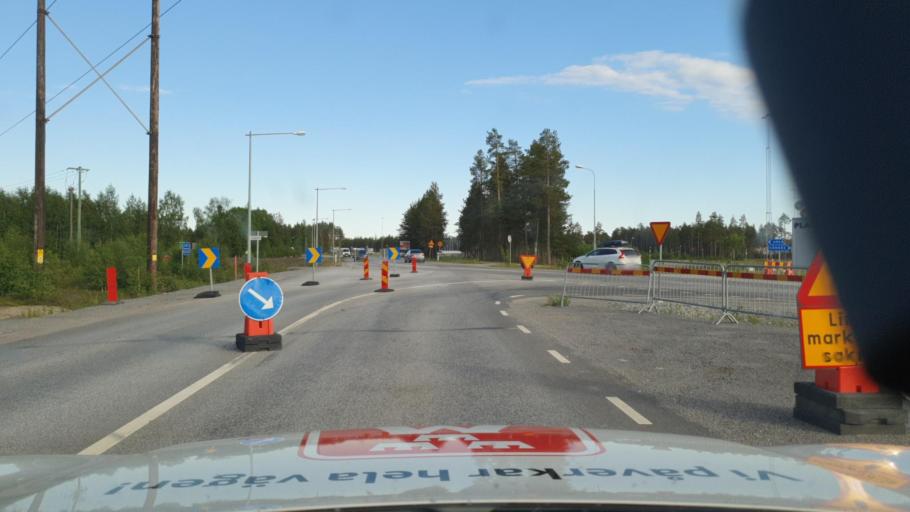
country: SE
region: Vaesterbotten
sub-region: Umea Kommun
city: Roback
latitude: 63.8487
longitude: 20.1572
